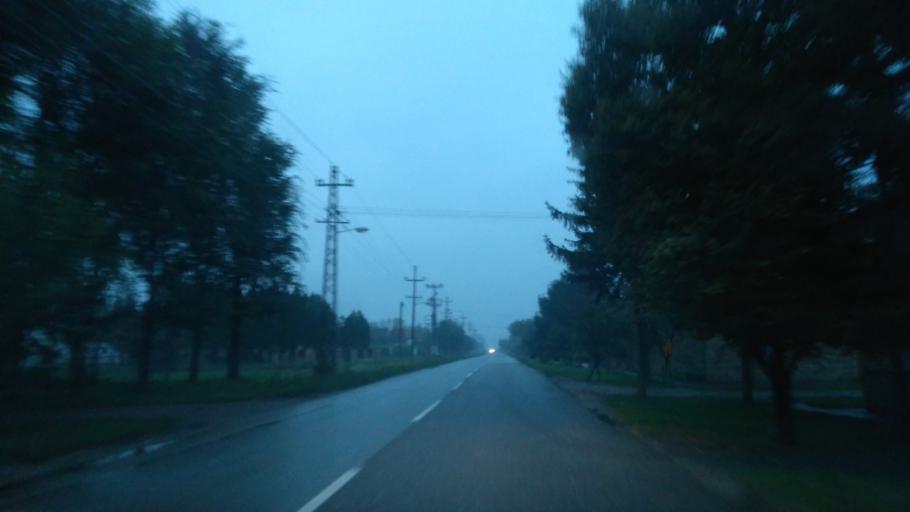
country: RS
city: Backo Petrovo Selo
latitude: 45.7169
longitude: 20.0917
